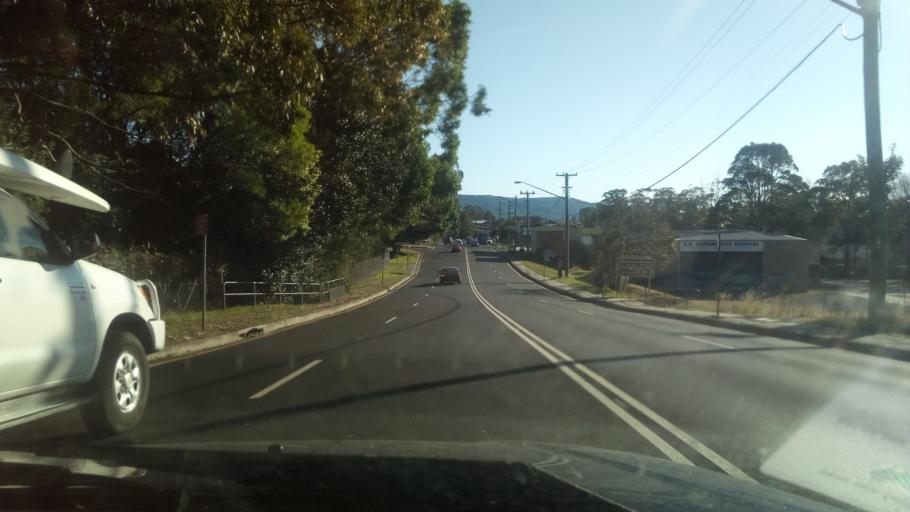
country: AU
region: New South Wales
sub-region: Wollongong
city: Corrimal
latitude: -34.3626
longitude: 150.8991
